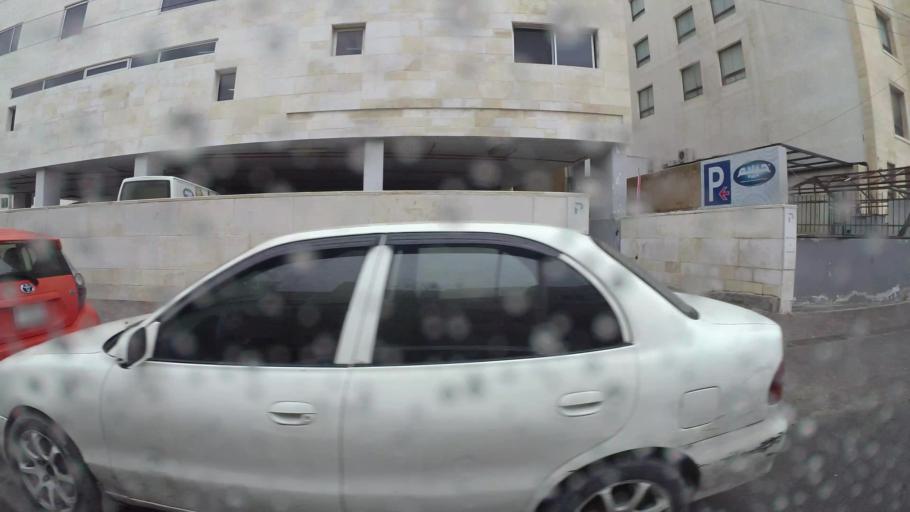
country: JO
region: Amman
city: Al Jubayhah
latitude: 31.9884
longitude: 35.8660
